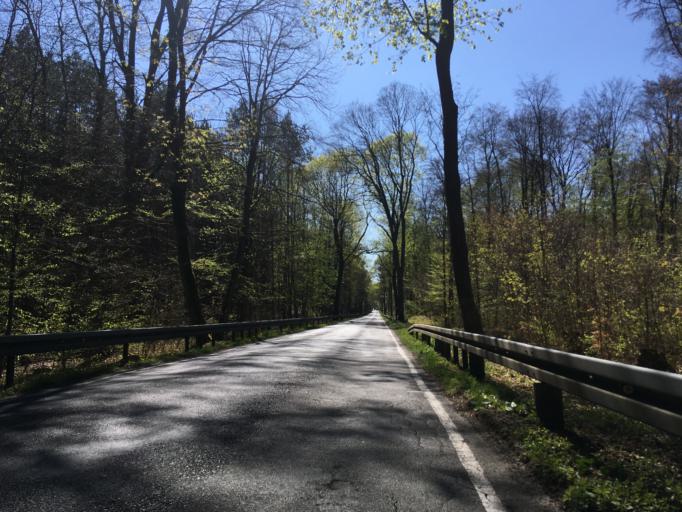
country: DE
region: Brandenburg
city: Bernau bei Berlin
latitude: 52.7222
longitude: 13.5694
